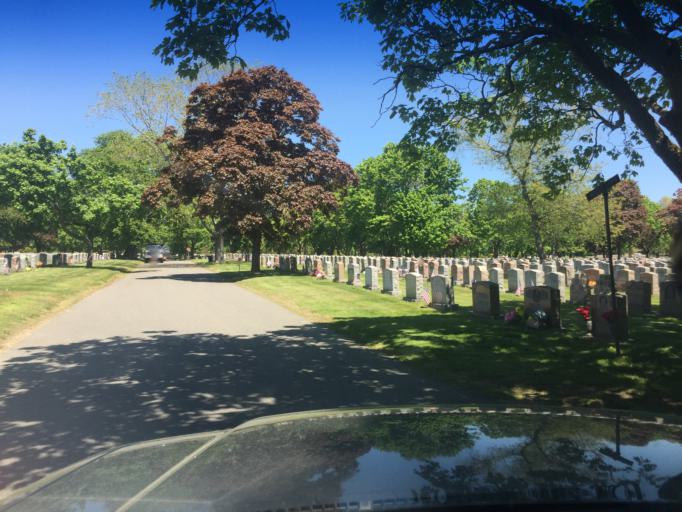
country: US
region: Massachusetts
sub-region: Middlesex County
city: Arlington
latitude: 42.4280
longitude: -71.1369
